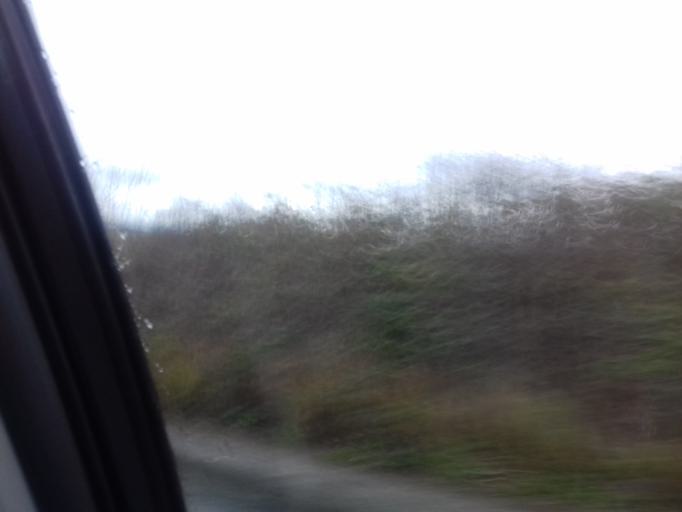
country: IE
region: Leinster
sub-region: Kilkenny
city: Graiguenamanagh
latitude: 52.6087
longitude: -6.9930
